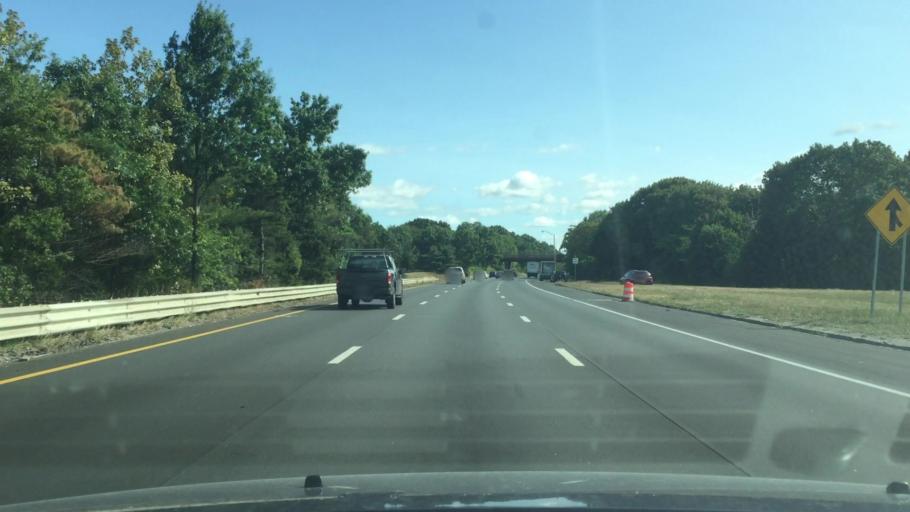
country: US
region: Massachusetts
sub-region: Essex County
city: Lawrence
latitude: 42.6651
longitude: -71.1927
